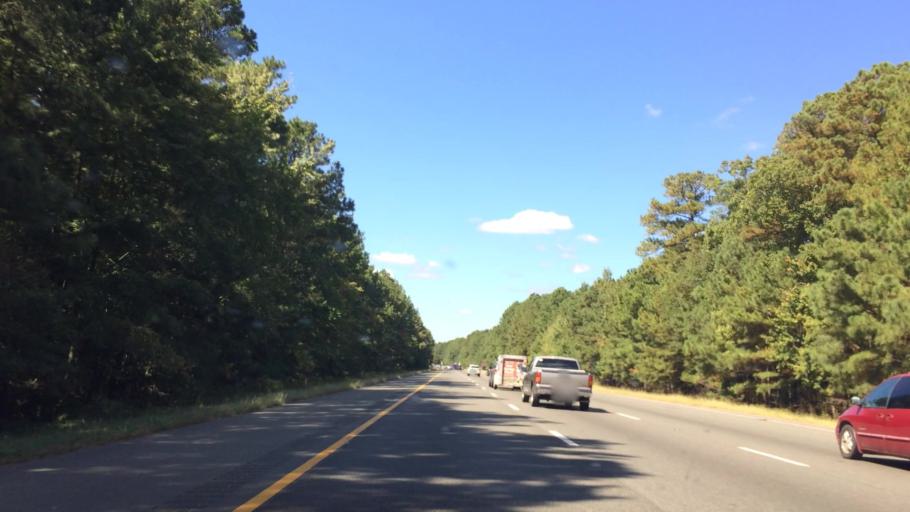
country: US
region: Virginia
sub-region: Henrico County
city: Glen Allen
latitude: 37.6710
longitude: -77.4905
